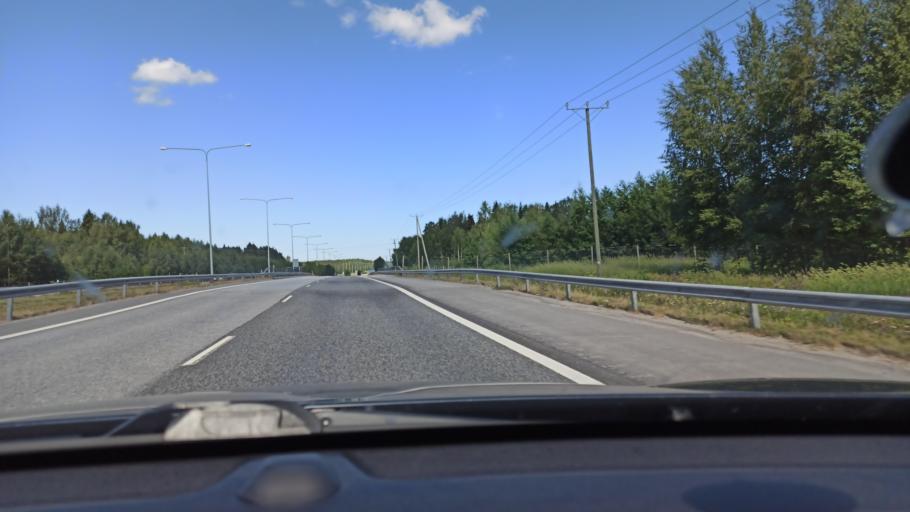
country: FI
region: Ostrobothnia
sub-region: Vaasa
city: Ristinummi
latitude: 63.0395
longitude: 21.7331
